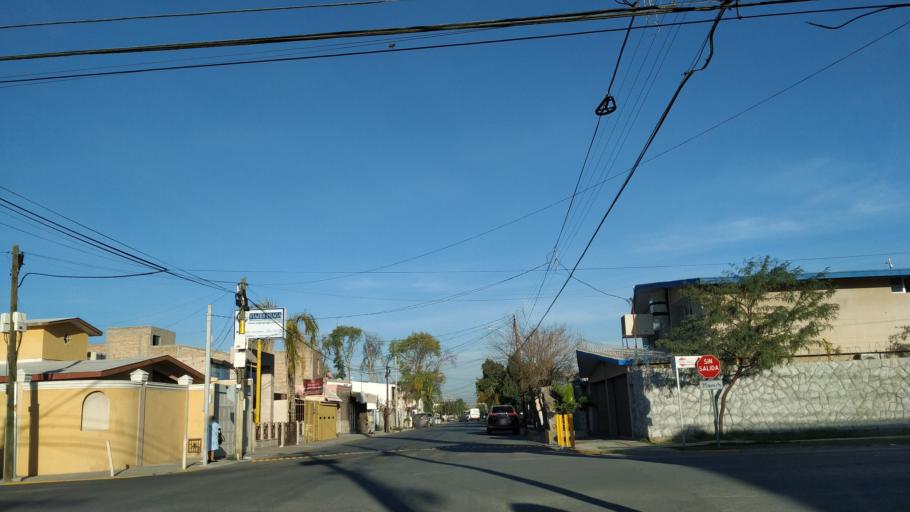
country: MX
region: Coahuila
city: Torreon
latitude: 25.5518
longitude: -103.4500
